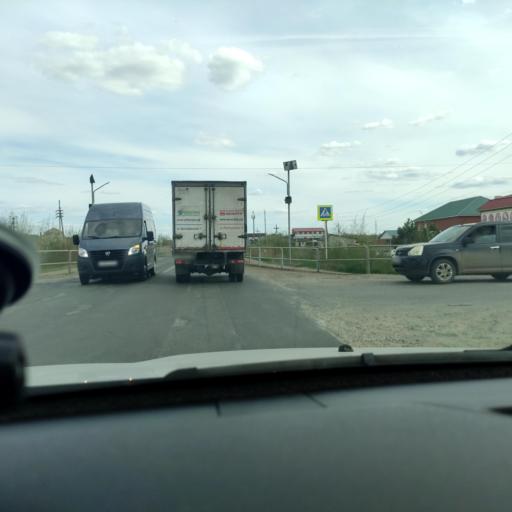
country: RU
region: Samara
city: Kinel'
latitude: 53.2142
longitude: 50.6143
